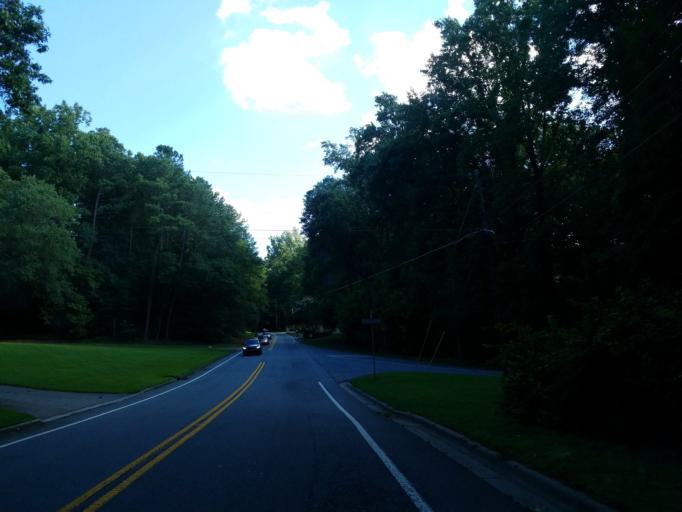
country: US
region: Georgia
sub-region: Fulton County
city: Sandy Springs
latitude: 33.9323
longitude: -84.4114
